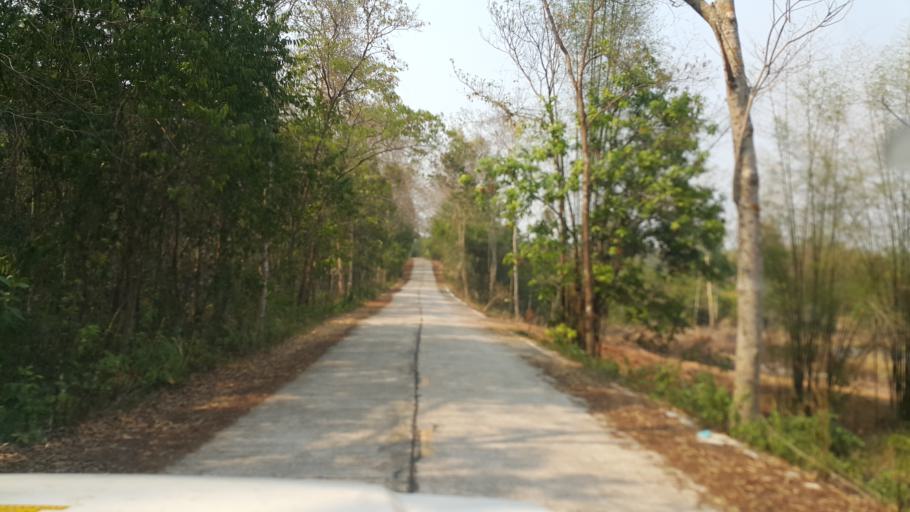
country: TH
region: Nakhon Phanom
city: Ban Phaeng
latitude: 17.9801
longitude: 104.1478
